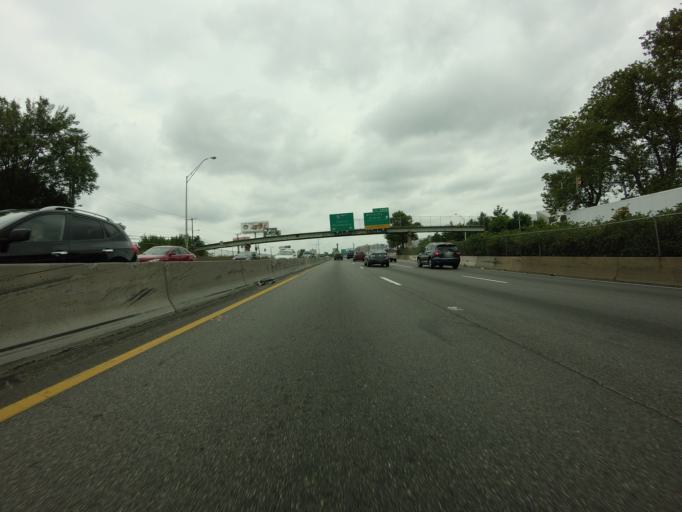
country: US
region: Pennsylvania
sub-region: Philadelphia County
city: Philadelphia
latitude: 39.9328
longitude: -75.2002
